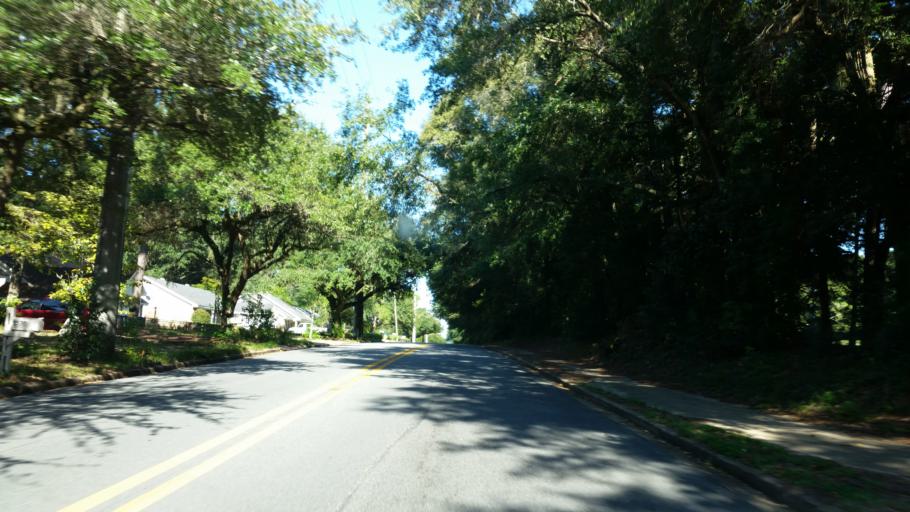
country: US
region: Alabama
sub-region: Mobile County
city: Prichard
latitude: 30.7052
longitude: -88.1714
